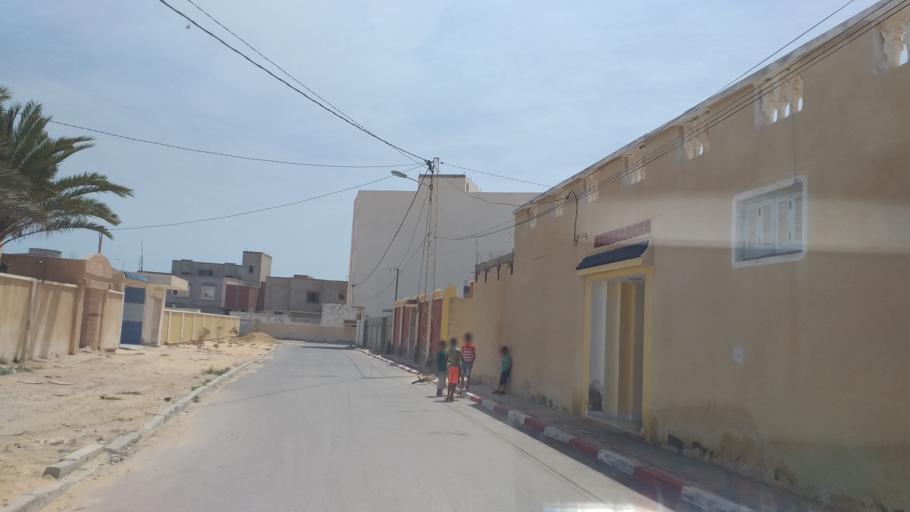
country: TN
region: Qabis
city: Gabes
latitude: 33.9470
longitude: 10.0676
